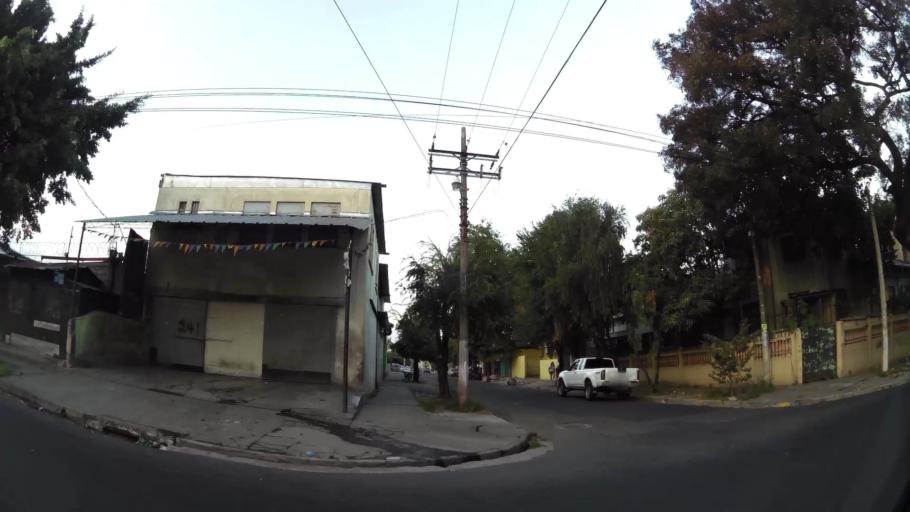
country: SV
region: San Salvador
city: San Salvador
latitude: 13.7096
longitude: -89.1868
